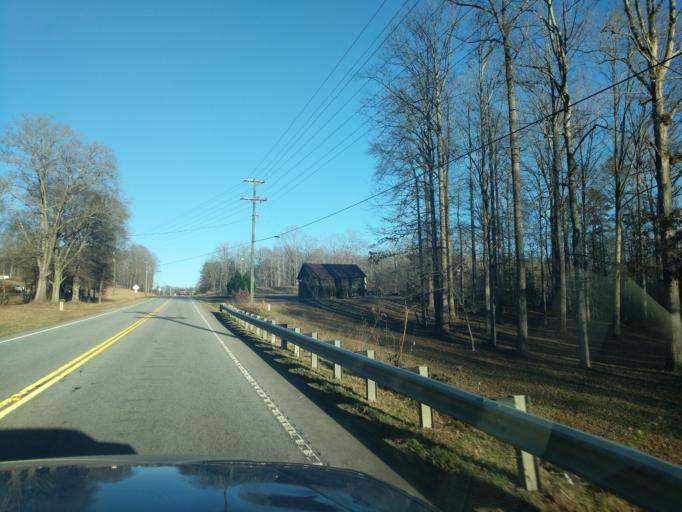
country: US
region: South Carolina
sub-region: Oconee County
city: Westminster
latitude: 34.6857
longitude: -83.1513
